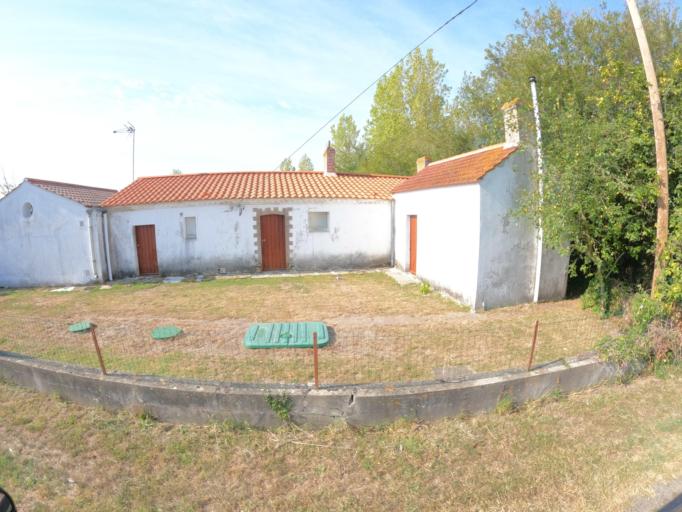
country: FR
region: Pays de la Loire
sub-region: Departement de la Vendee
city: Saint-Jean-de-Monts
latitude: 46.7991
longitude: -2.0539
